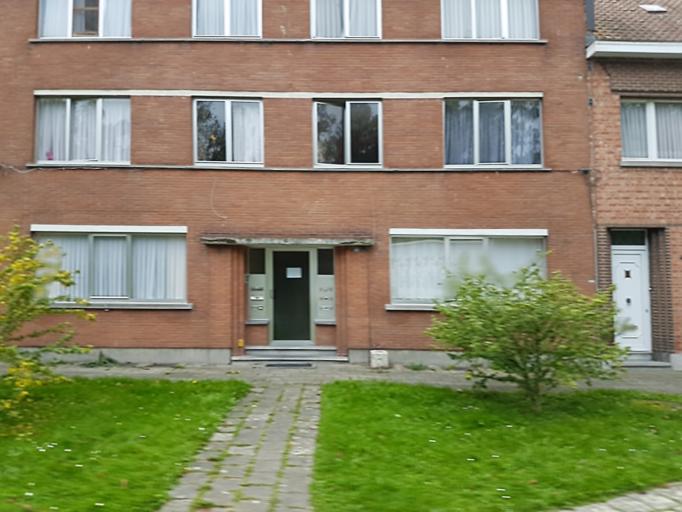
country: BE
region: Flanders
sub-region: Provincie Antwerpen
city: Zwijndrecht
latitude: 51.2070
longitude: 4.3510
